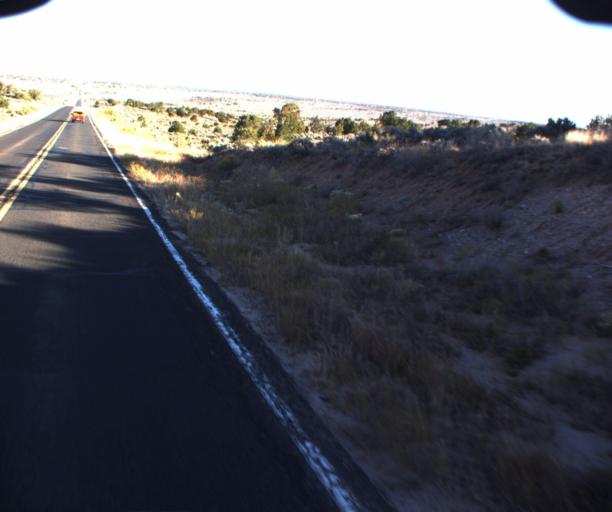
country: US
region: Arizona
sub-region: Apache County
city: Ganado
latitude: 35.5906
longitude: -109.5379
